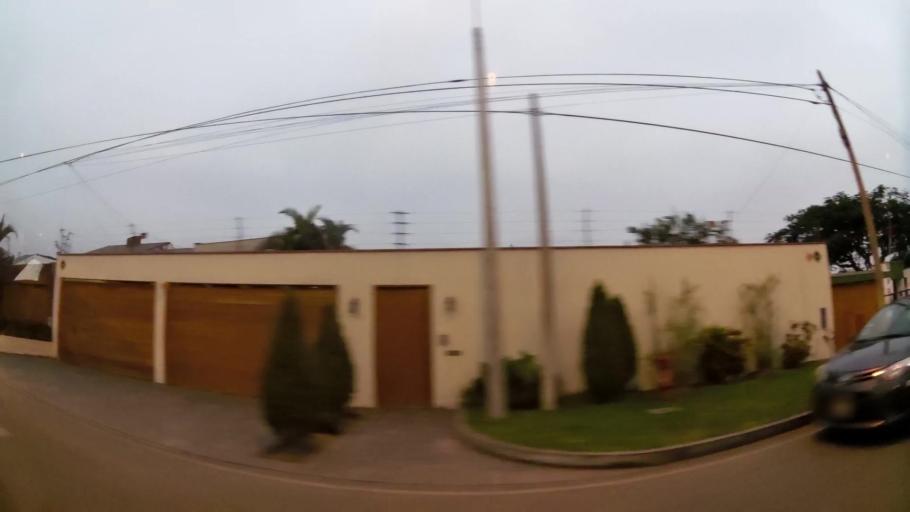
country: PE
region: Lima
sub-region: Lima
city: La Molina
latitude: -12.0880
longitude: -76.9502
